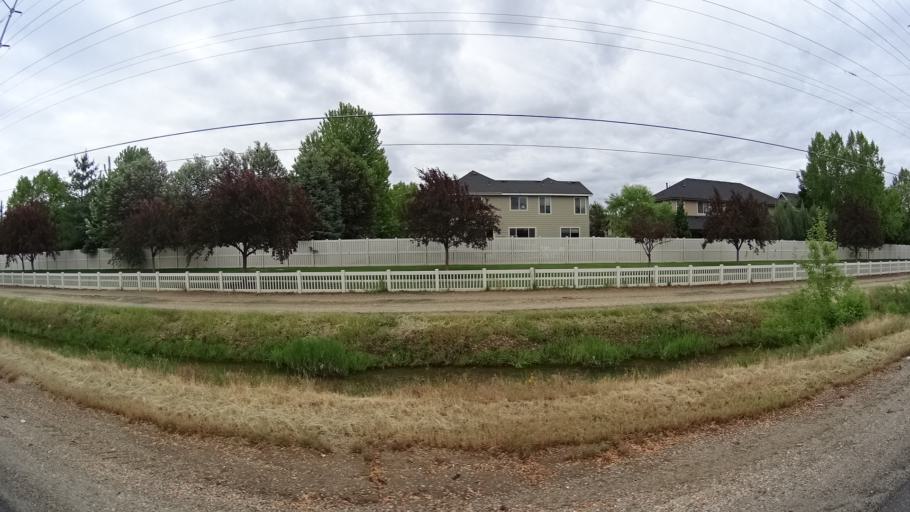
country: US
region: Idaho
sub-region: Ada County
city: Meridian
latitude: 43.6484
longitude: -116.4180
